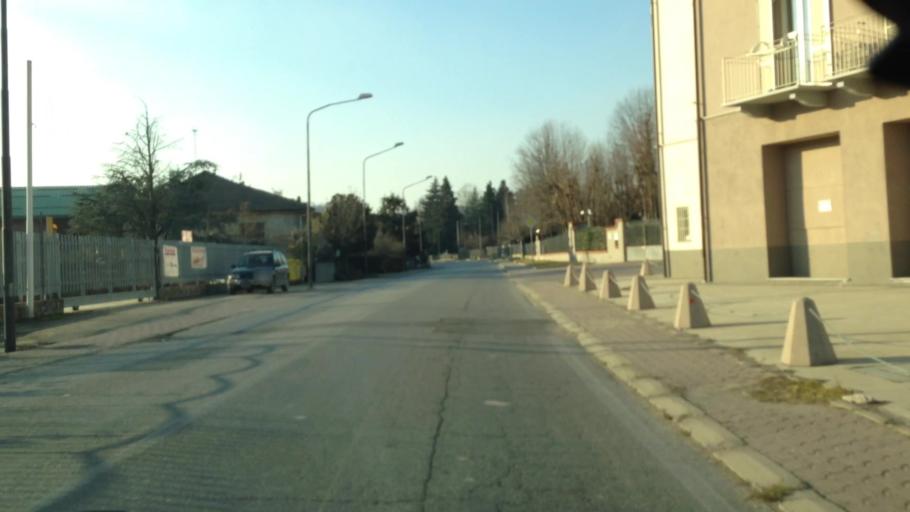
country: IT
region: Piedmont
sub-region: Provincia di Asti
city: Mombercelli
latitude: 44.8230
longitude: 8.2922
